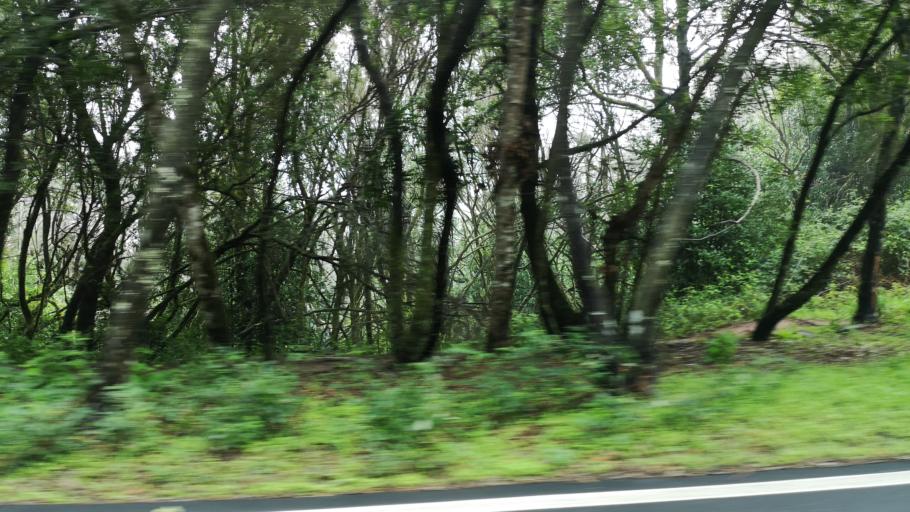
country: ES
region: Canary Islands
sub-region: Provincia de Santa Cruz de Tenerife
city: Vallehermosa
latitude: 28.1258
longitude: -17.2534
